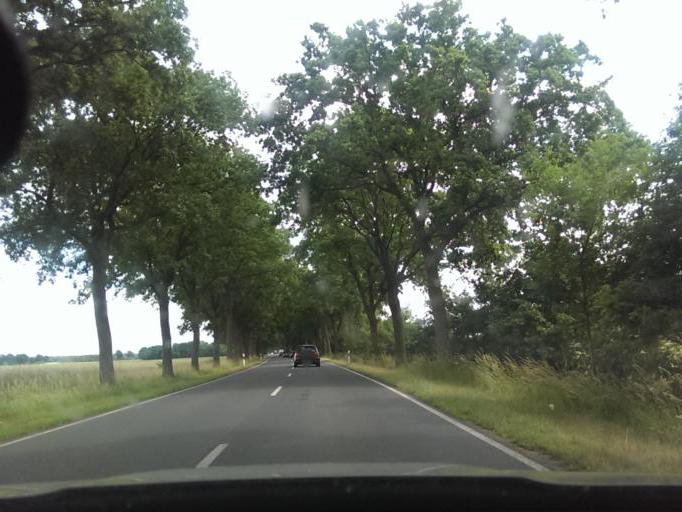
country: DE
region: Lower Saxony
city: Essel
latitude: 52.6719
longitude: 9.6568
